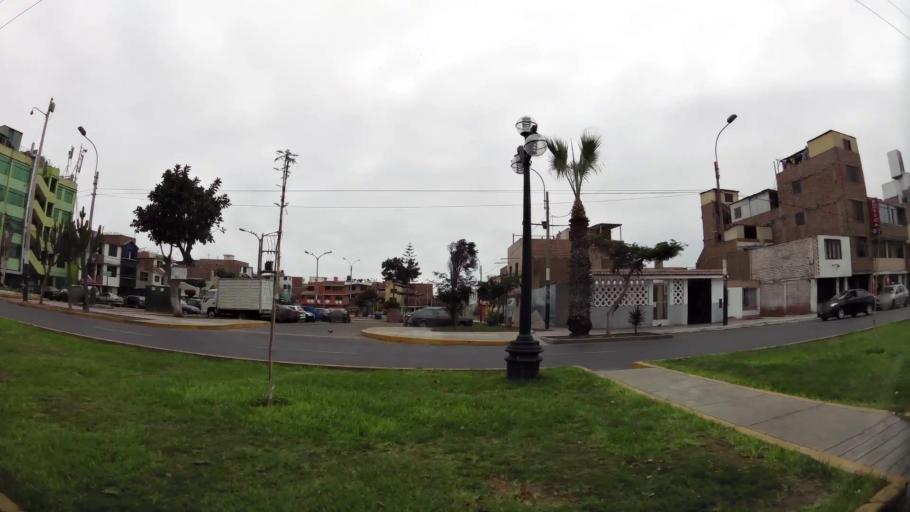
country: PE
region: Callao
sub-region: Callao
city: Callao
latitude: -12.0606
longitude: -77.1050
